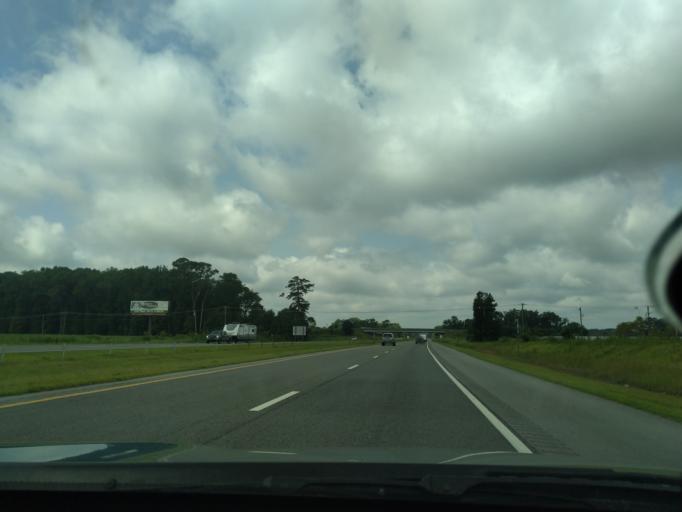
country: US
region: North Carolina
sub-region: Martin County
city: Robersonville
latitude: 35.8341
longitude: -77.2628
